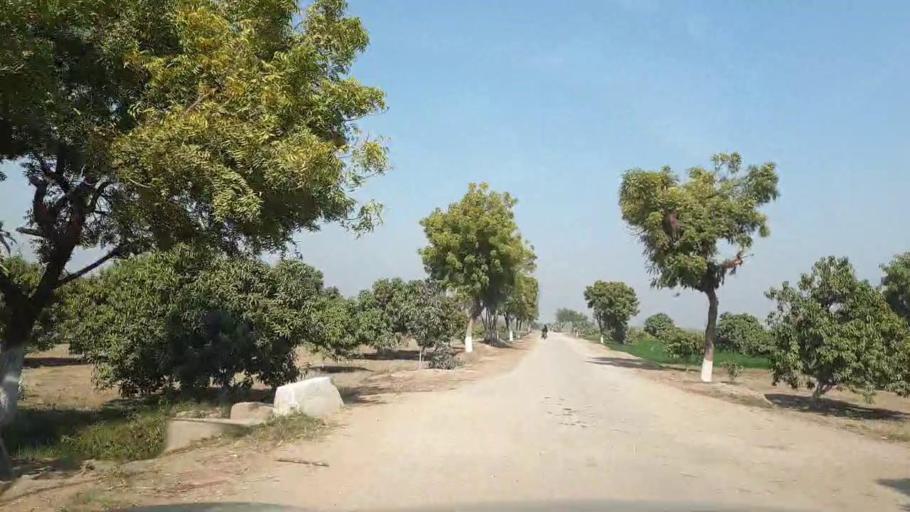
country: PK
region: Sindh
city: Tando Adam
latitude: 25.6282
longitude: 68.7383
